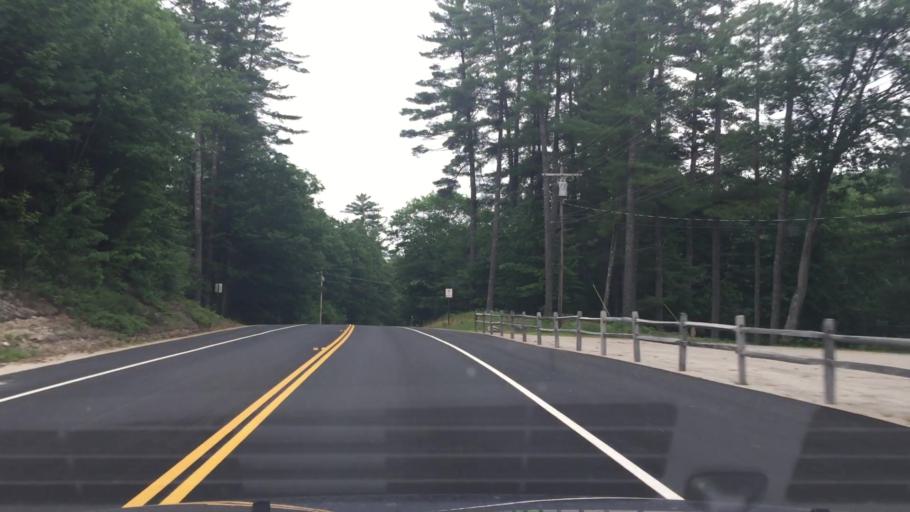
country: US
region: New Hampshire
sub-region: Carroll County
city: Madison
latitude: 43.8677
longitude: -71.0887
